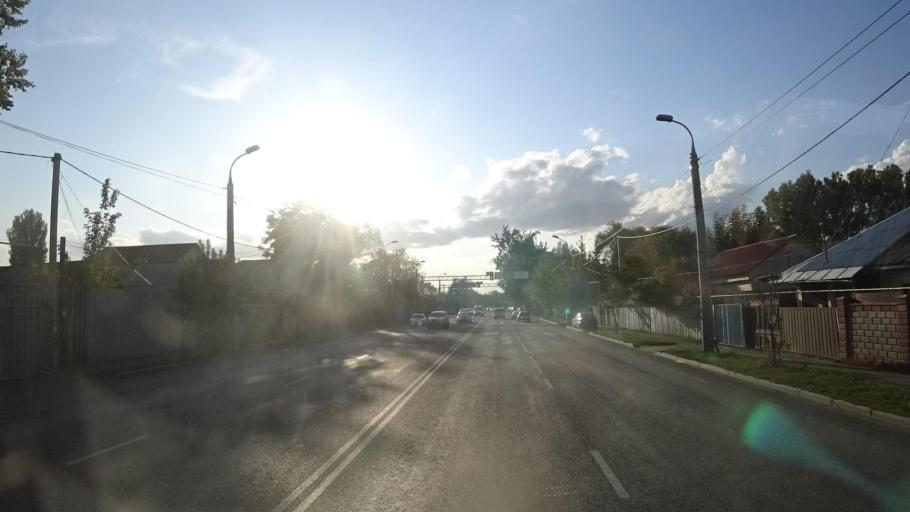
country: KZ
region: Almaty Oblysy
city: Pervomayskiy
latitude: 43.3217
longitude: 76.9684
